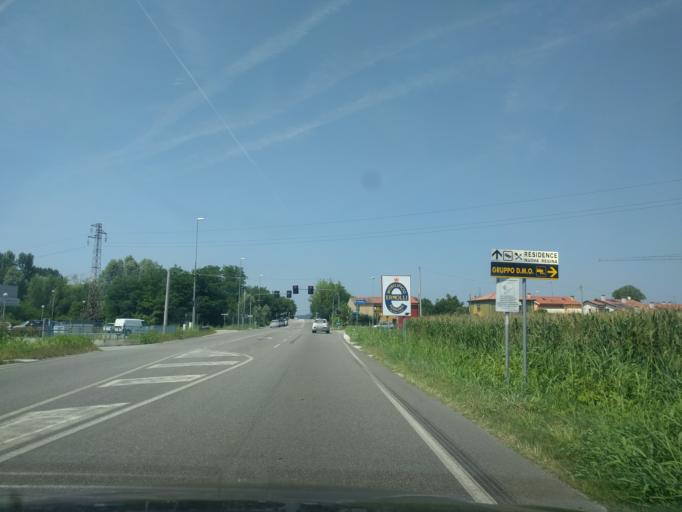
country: IT
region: Veneto
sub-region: Provincia di Padova
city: Monselice
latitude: 45.2462
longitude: 11.7589
